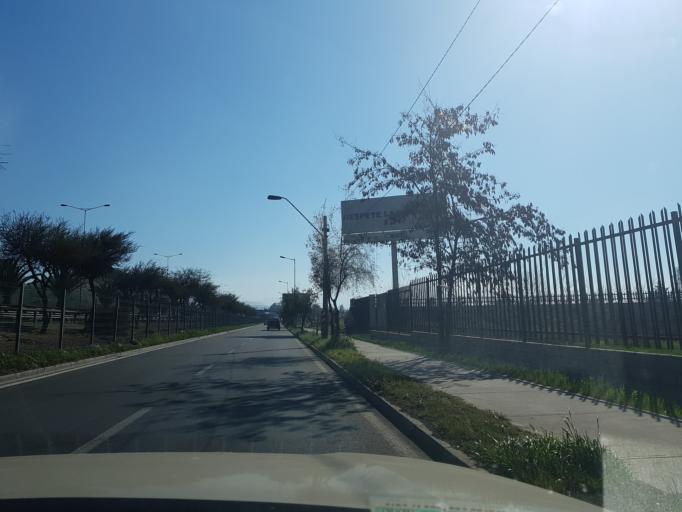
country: CL
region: Santiago Metropolitan
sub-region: Provincia de Santiago
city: Lo Prado
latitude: -33.3725
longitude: -70.7274
